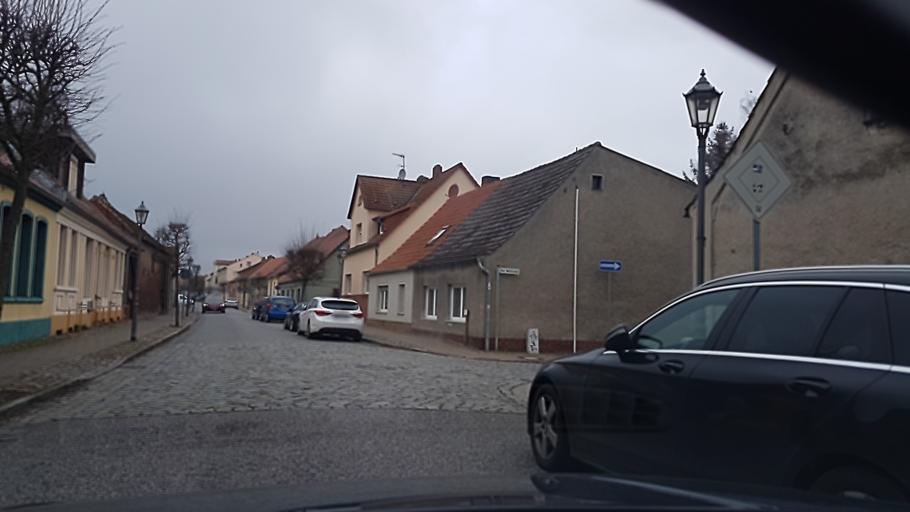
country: DE
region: Brandenburg
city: Kremmen
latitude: 52.7590
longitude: 13.0303
